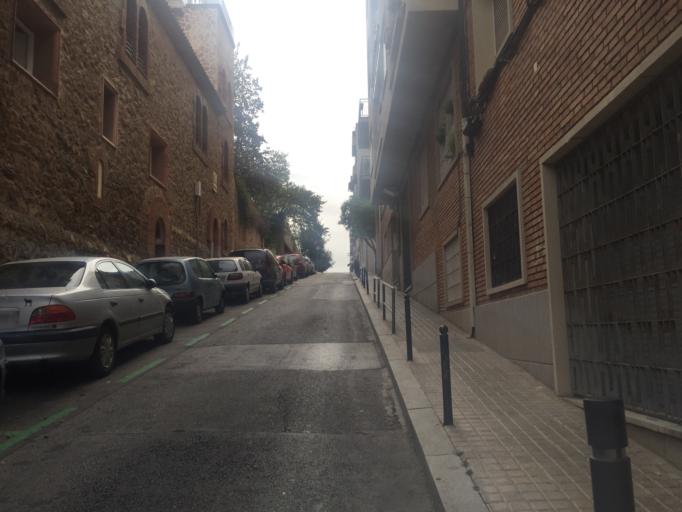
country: ES
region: Catalonia
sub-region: Provincia de Barcelona
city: Sarria-Sant Gervasi
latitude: 41.4108
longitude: 2.1422
